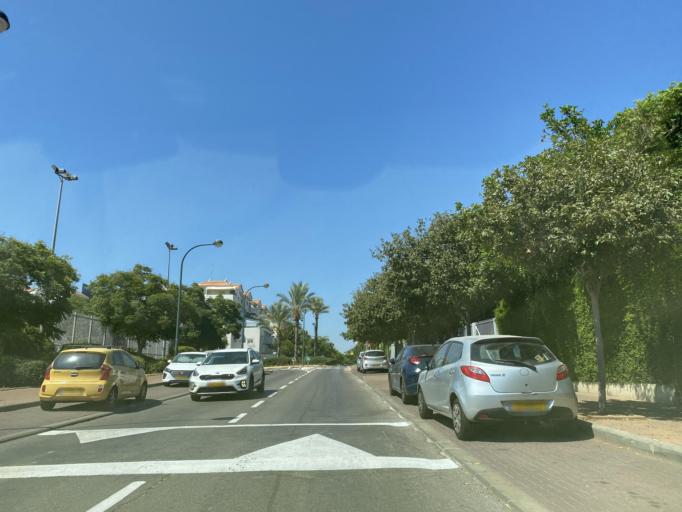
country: IL
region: Central District
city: Ra'anana
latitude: 32.1871
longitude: 34.8869
